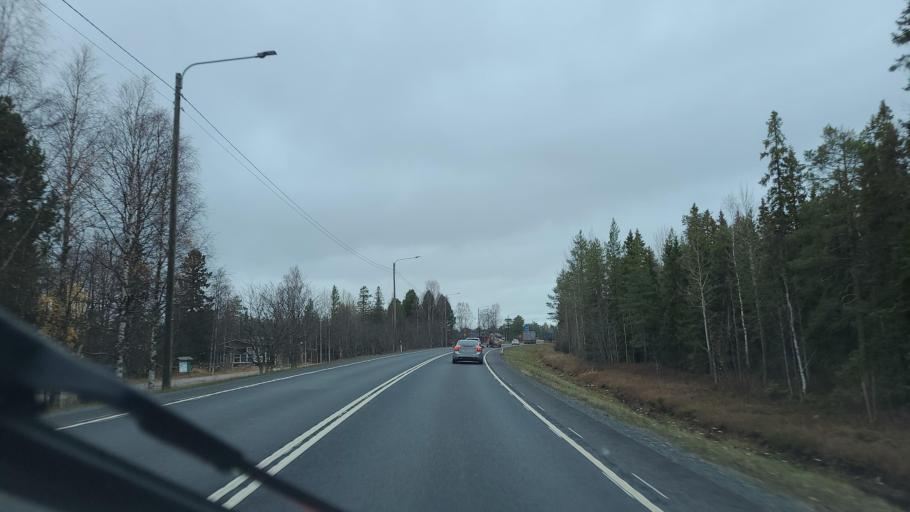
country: FI
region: Northern Ostrobothnia
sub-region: Oulunkaari
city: Kuivaniemi
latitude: 65.5236
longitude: 25.2619
